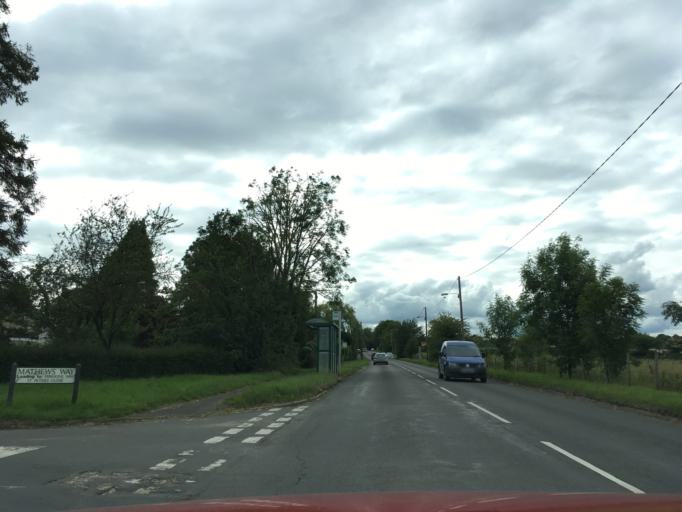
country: GB
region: England
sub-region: Oxfordshire
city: Boars Hill
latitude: 51.7034
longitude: -1.3084
